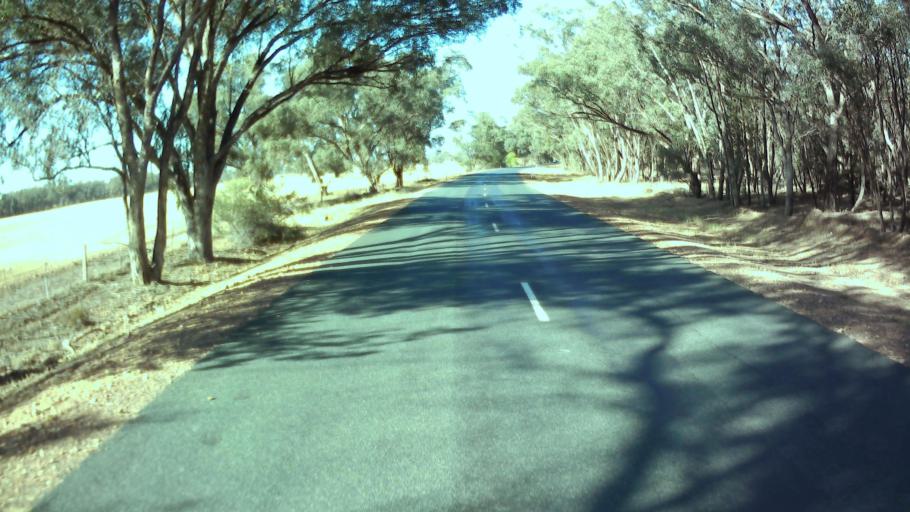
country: AU
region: New South Wales
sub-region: Weddin
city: Grenfell
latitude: -34.0092
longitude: 148.1204
